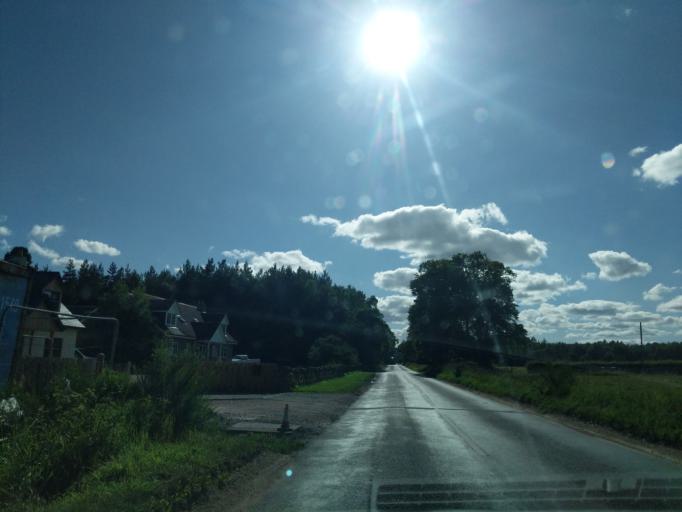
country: GB
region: Scotland
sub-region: Aberdeenshire
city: Torphins
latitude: 57.0228
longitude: -2.6214
